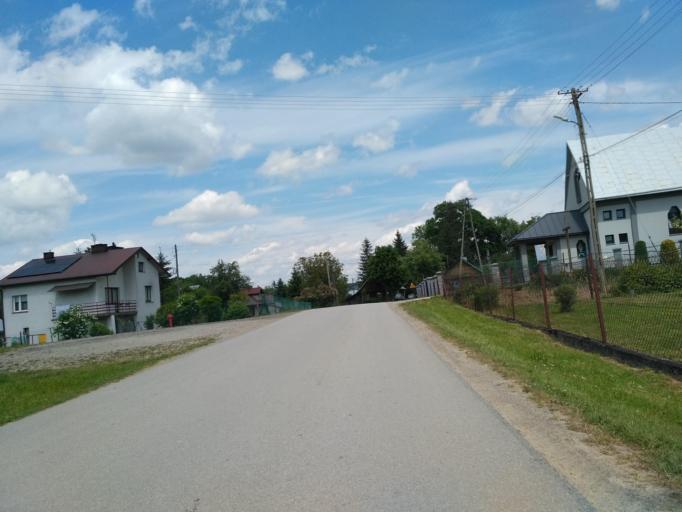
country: PL
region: Subcarpathian Voivodeship
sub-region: Powiat krosnienski
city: Dukla
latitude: 49.5874
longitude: 21.6217
